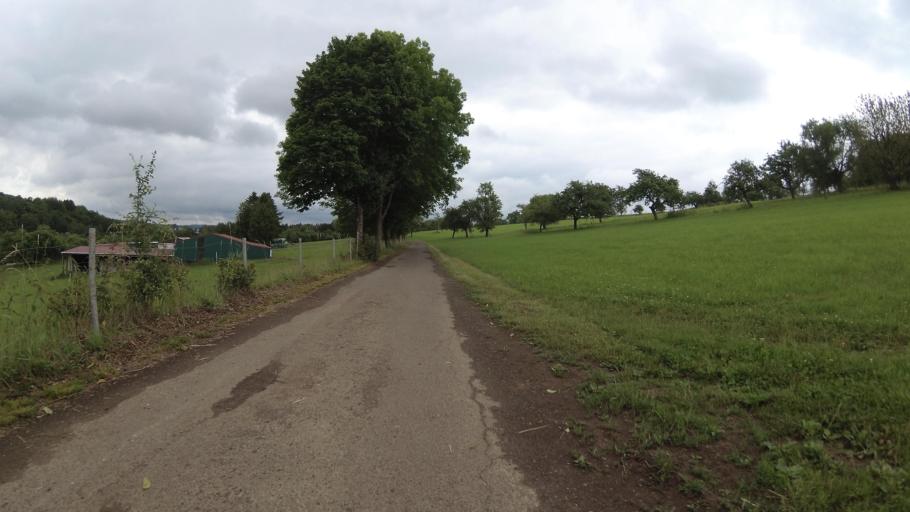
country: DE
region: Saarland
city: Oberthal
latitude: 49.5056
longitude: 7.0731
